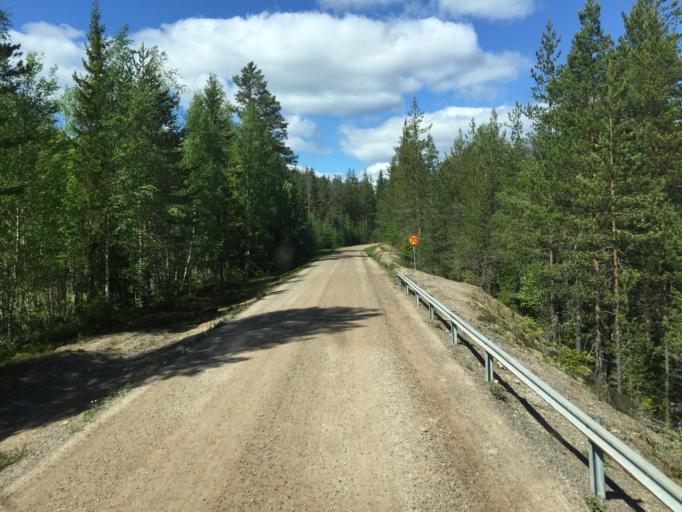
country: SE
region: Dalarna
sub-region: Vansbro Kommun
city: Vansbro
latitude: 60.4276
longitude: 14.2300
